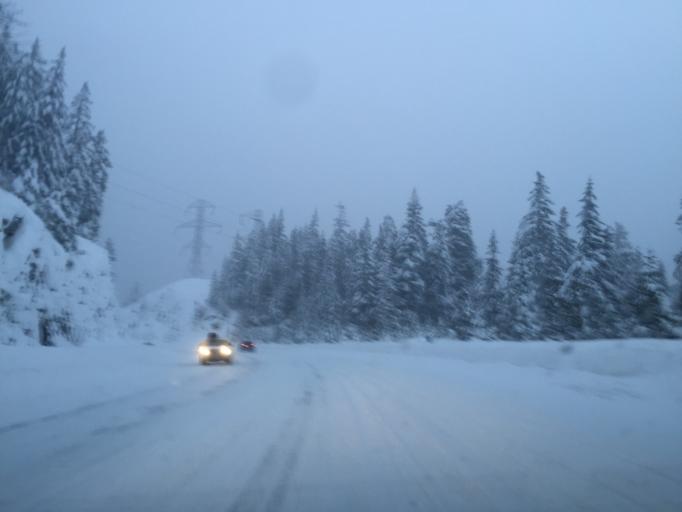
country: US
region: Washington
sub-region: Chelan County
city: Leavenworth
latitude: 47.7829
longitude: -120.8953
